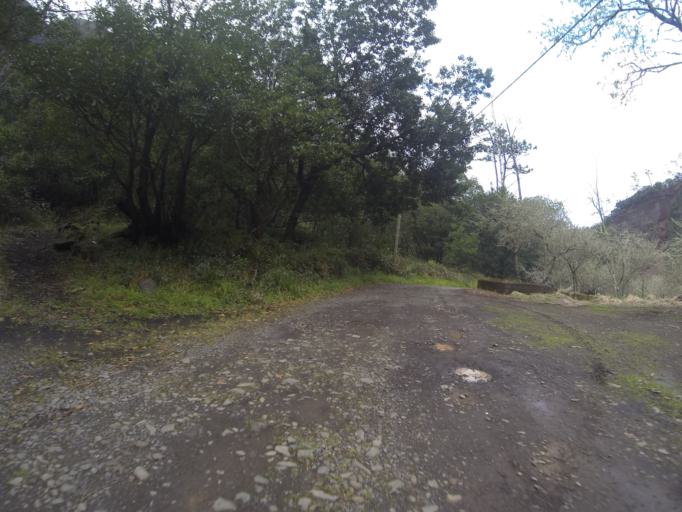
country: PT
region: Madeira
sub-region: Sao Vicente
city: Sao Vicente
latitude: 32.7992
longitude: -17.1151
